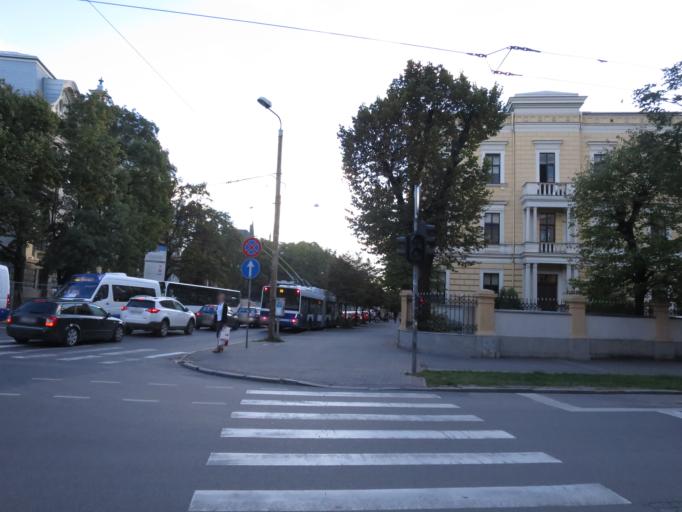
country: LV
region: Riga
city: Riga
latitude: 56.9565
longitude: 24.1137
